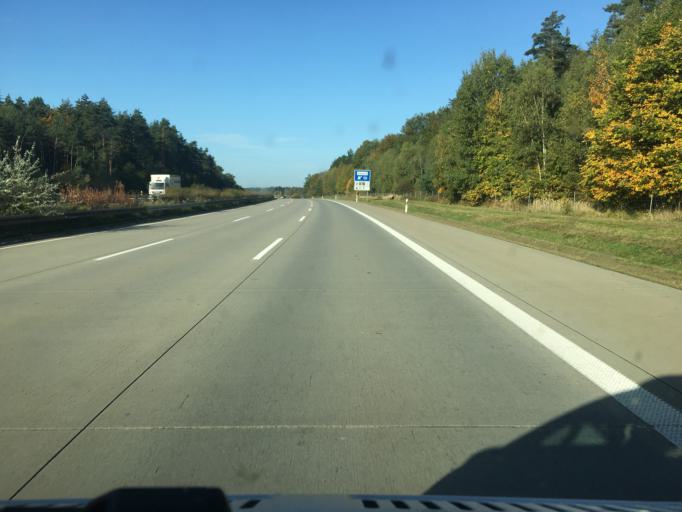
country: DE
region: Thuringia
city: Kraftsdorf
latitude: 50.8923
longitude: 11.9141
